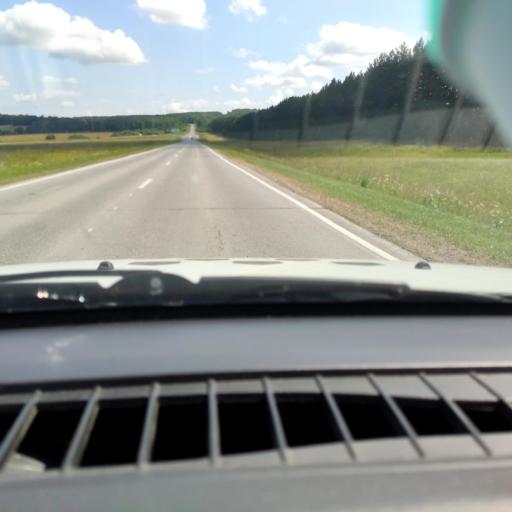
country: RU
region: Bashkortostan
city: Verkhniye Kigi
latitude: 55.3934
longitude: 58.6495
